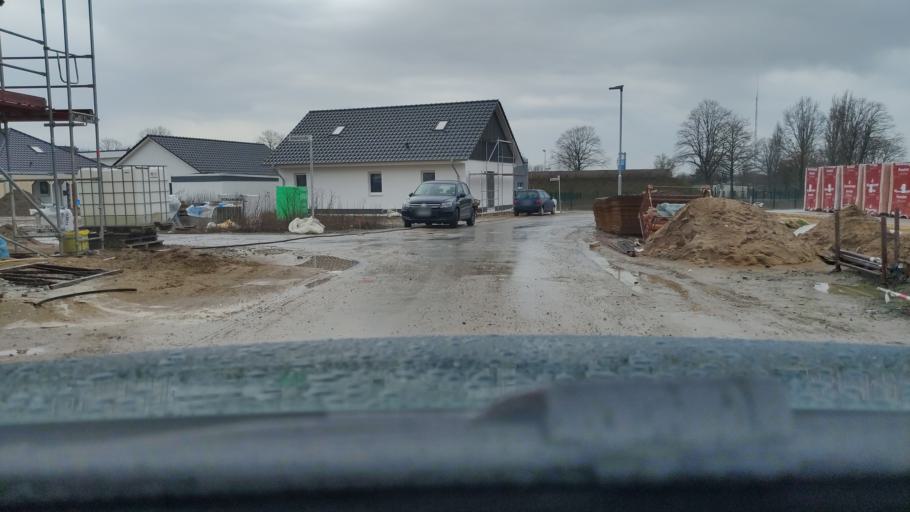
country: DE
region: Lower Saxony
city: Ilsede
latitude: 52.2736
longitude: 10.2264
